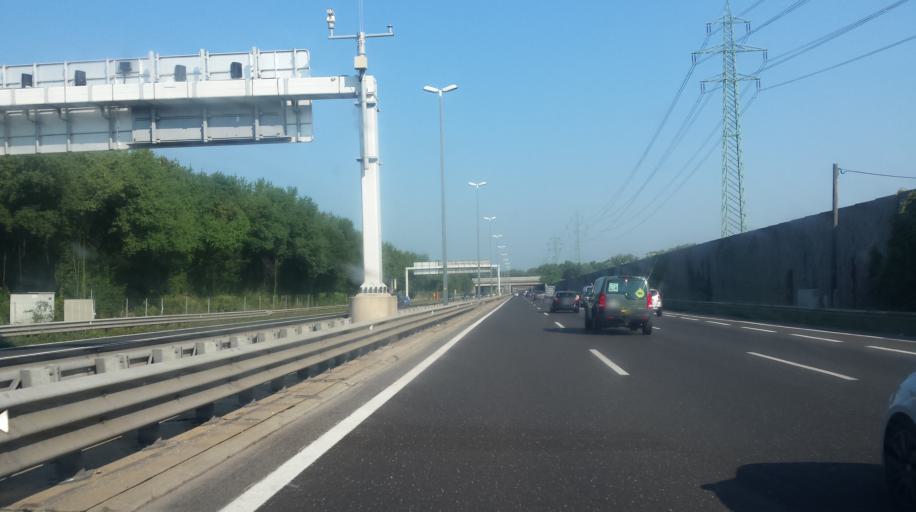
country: AT
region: Lower Austria
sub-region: Politischer Bezirk Korneuburg
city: Langenzersdorf
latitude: 48.2616
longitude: 16.3813
